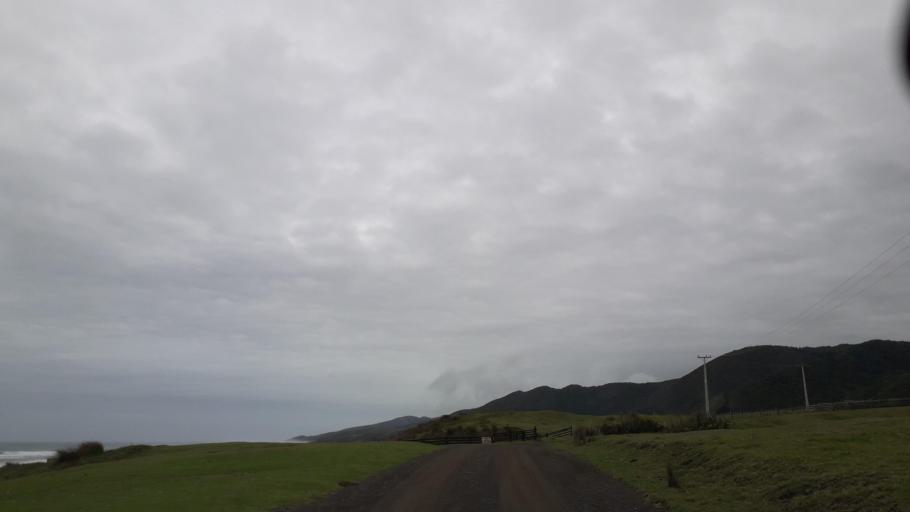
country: NZ
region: Northland
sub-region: Far North District
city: Ahipara
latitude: -35.4291
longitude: 173.2709
